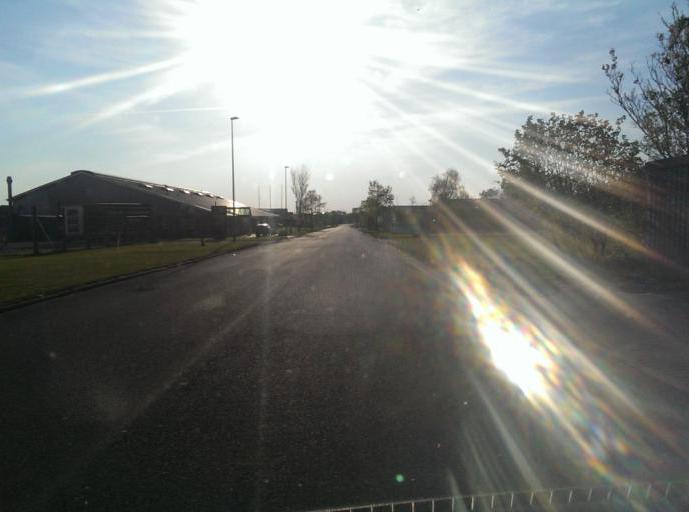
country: DK
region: South Denmark
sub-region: Esbjerg Kommune
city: Bramming
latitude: 55.4672
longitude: 8.6757
